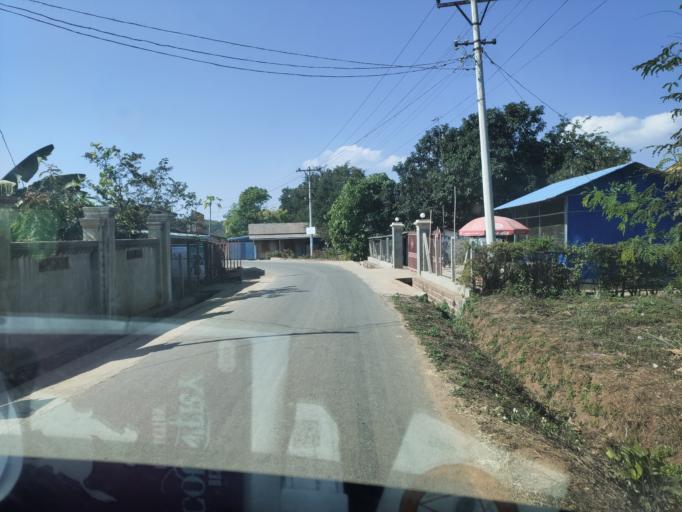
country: MM
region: Mandalay
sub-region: Pyin Oo Lwin District
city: Pyin Oo Lwin
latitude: 21.9539
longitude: 96.3906
